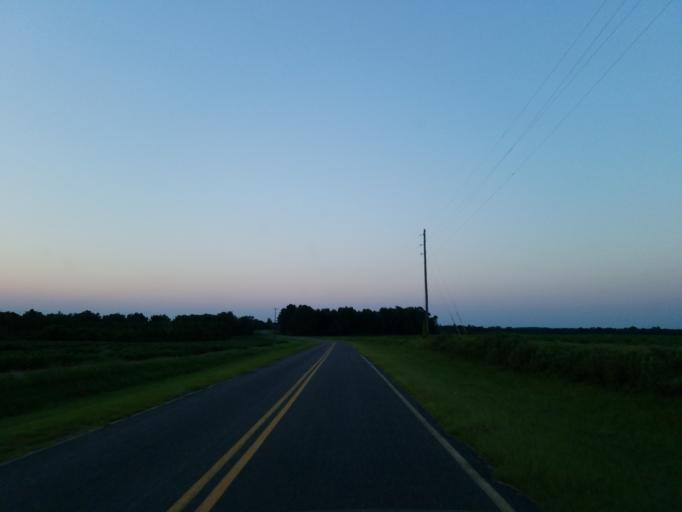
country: US
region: Georgia
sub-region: Dooly County
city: Unadilla
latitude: 32.1936
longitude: -83.7972
